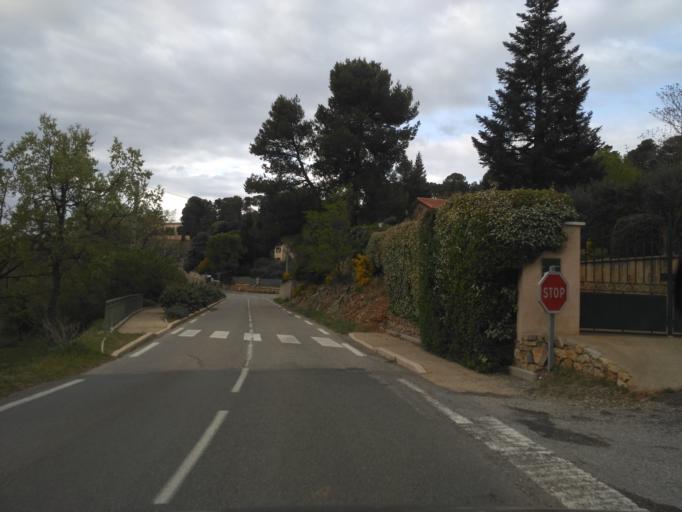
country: FR
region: Provence-Alpes-Cote d'Azur
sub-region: Departement du Var
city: Saint-Julien
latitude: 43.6346
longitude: 5.9379
